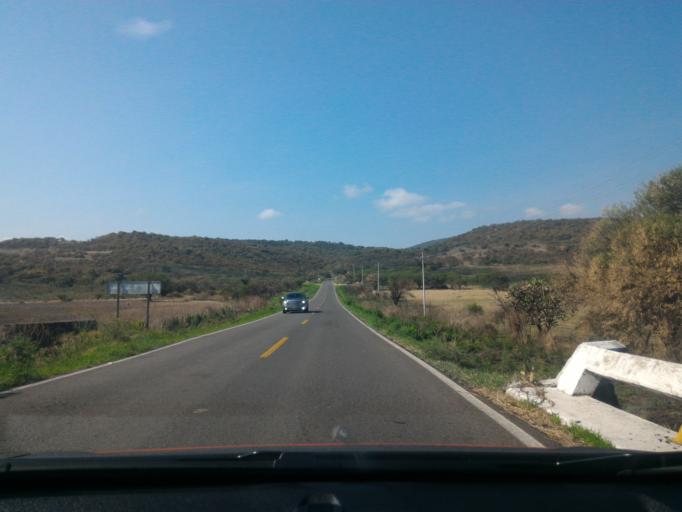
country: MX
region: Guanajuato
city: Ciudad Manuel Doblado
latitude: 20.6073
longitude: -101.9907
